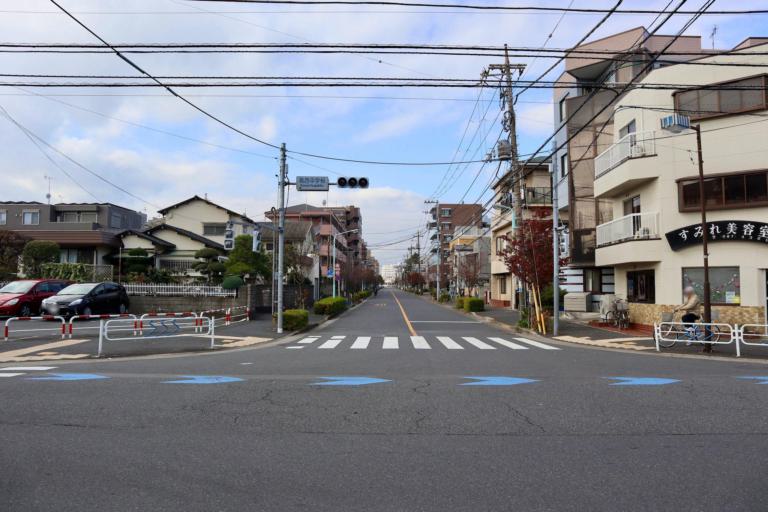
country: JP
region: Tokyo
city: Urayasu
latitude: 35.6710
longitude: 139.8722
